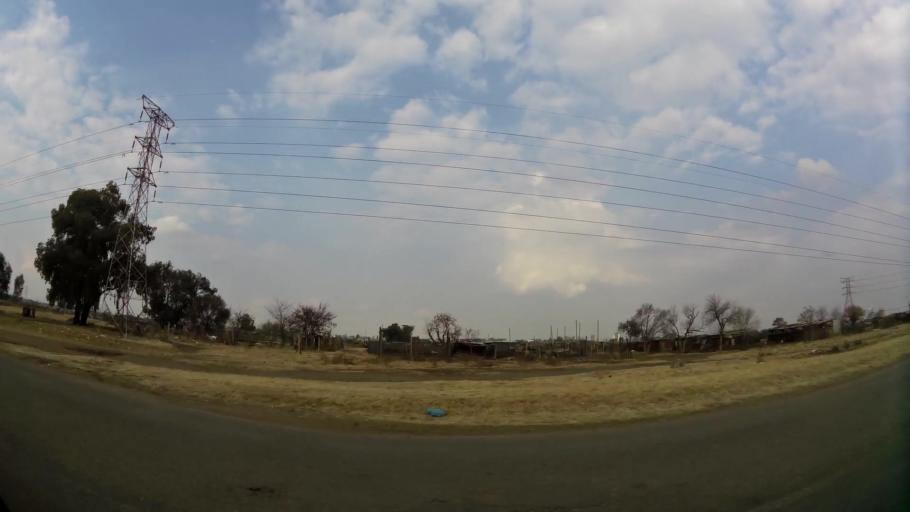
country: ZA
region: Gauteng
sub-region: Sedibeng District Municipality
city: Vereeniging
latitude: -26.6733
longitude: 27.8986
